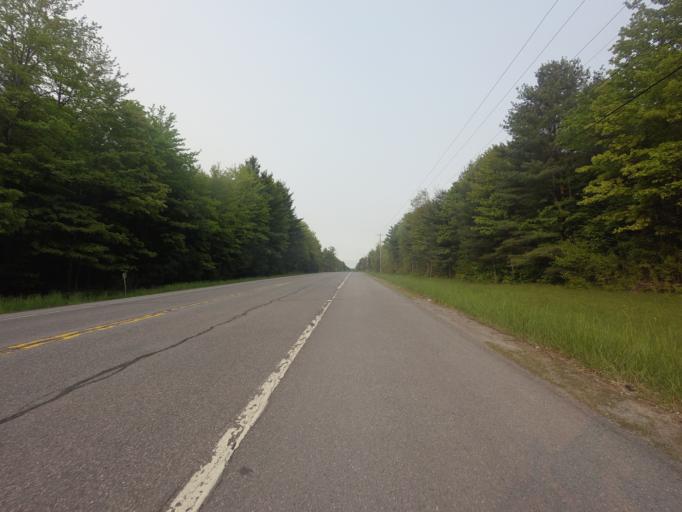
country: US
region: New York
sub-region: Jefferson County
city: Carthage
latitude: 44.0928
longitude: -75.4214
